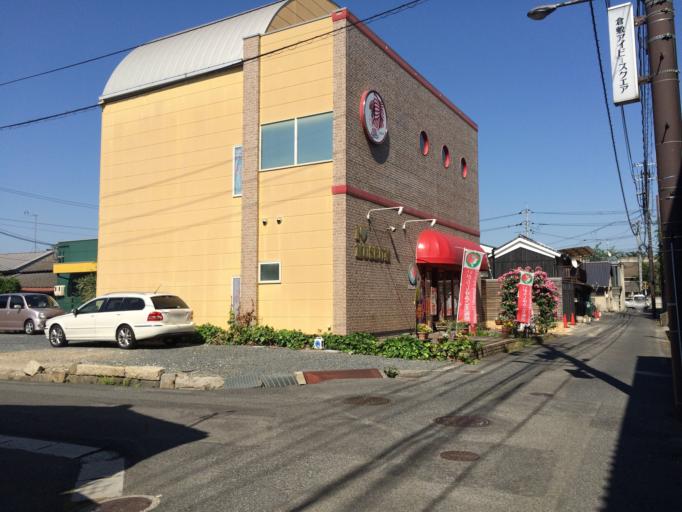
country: JP
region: Okayama
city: Kurashiki
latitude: 34.5956
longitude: 133.7737
